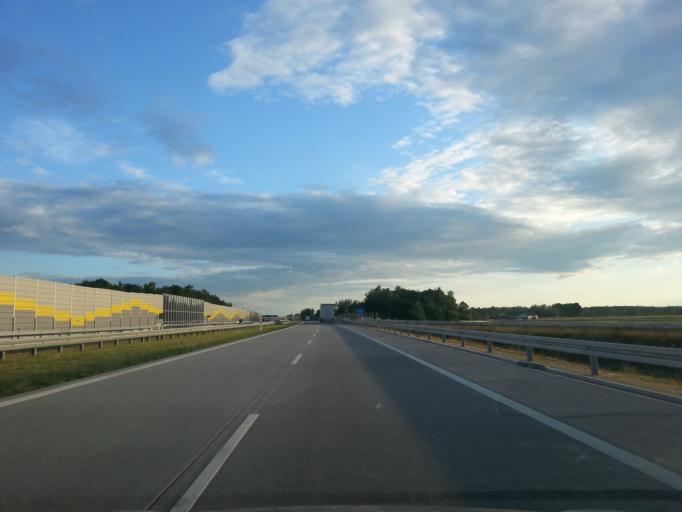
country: PL
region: Lodz Voivodeship
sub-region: Powiat sieradzki
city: Zloczew
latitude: 51.3846
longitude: 18.5572
